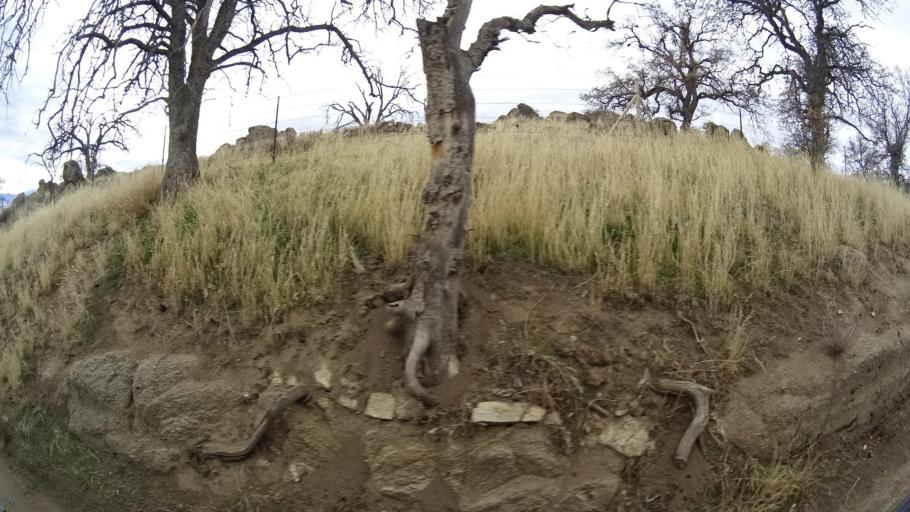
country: US
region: California
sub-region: Kern County
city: Stallion Springs
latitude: 35.1235
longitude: -118.7251
